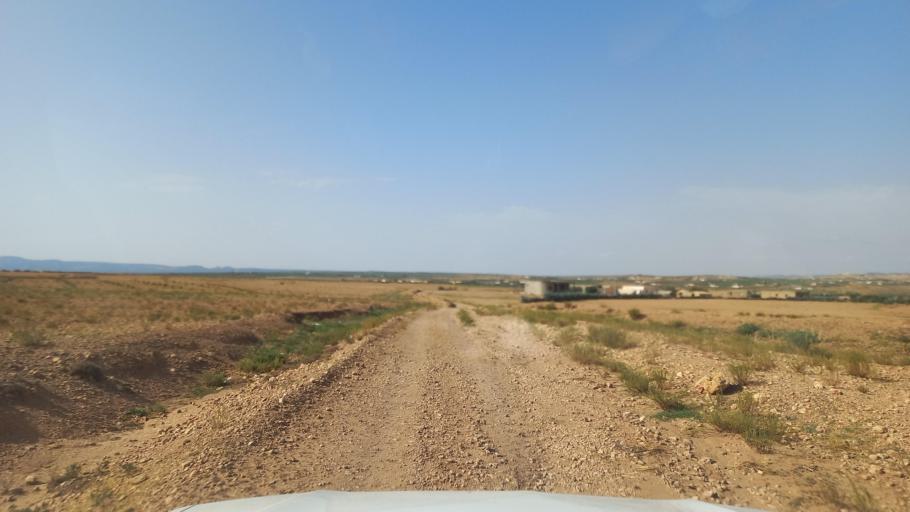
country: TN
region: Al Qasrayn
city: Kasserine
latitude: 35.3405
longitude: 8.8198
